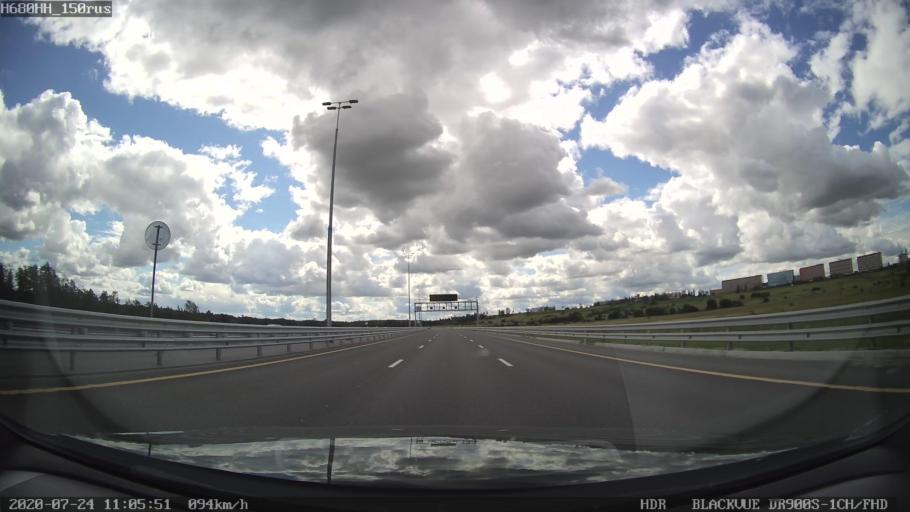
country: RU
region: St.-Petersburg
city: Shushary
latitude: 59.7715
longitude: 30.3630
